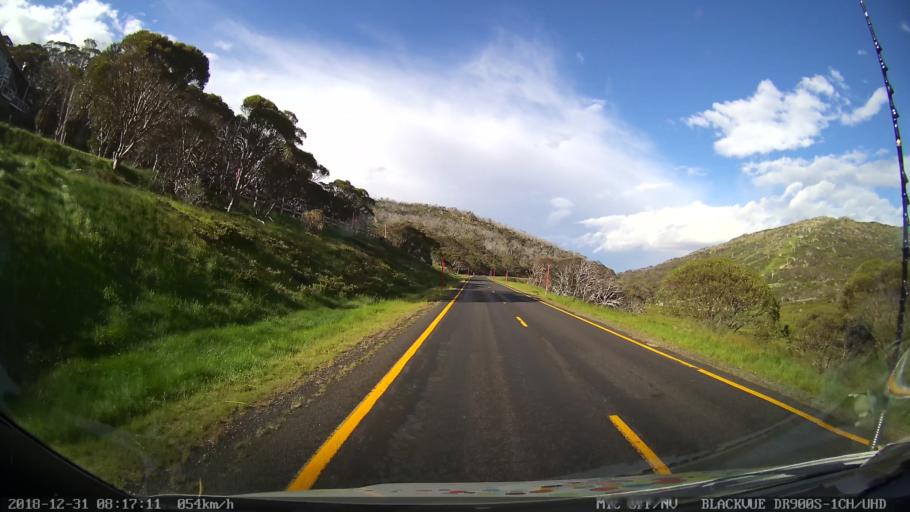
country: AU
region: New South Wales
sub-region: Snowy River
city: Jindabyne
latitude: -36.4091
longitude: 148.4064
